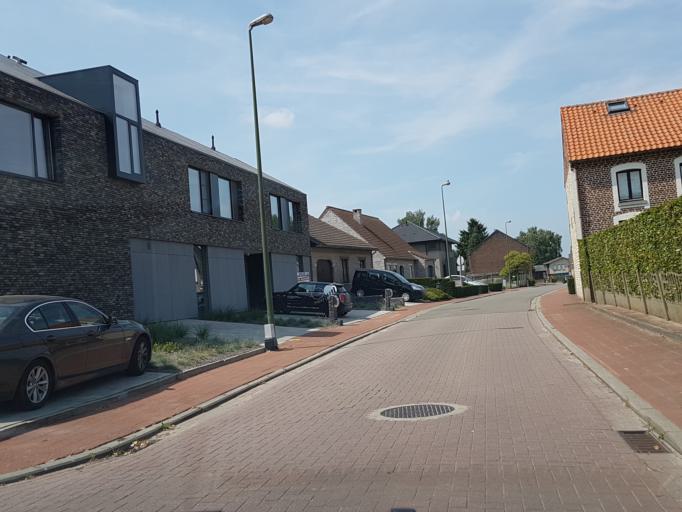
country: BE
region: Flanders
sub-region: Provincie Vlaams-Brabant
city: Kampenhout
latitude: 50.9225
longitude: 4.5688
